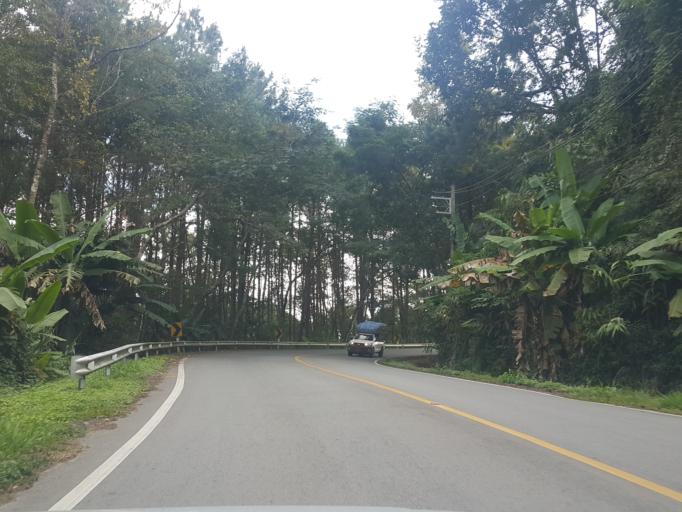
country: TH
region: Chiang Mai
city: Mae Chaem
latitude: 18.5204
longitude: 98.5179
